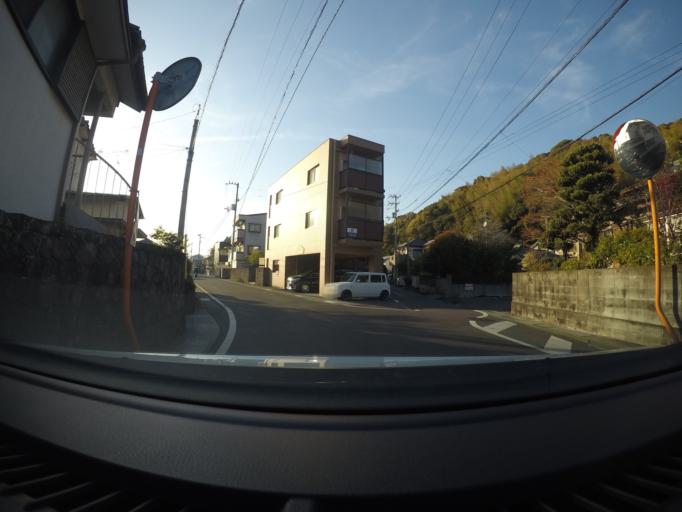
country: JP
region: Kochi
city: Kochi-shi
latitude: 33.5429
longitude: 133.5738
